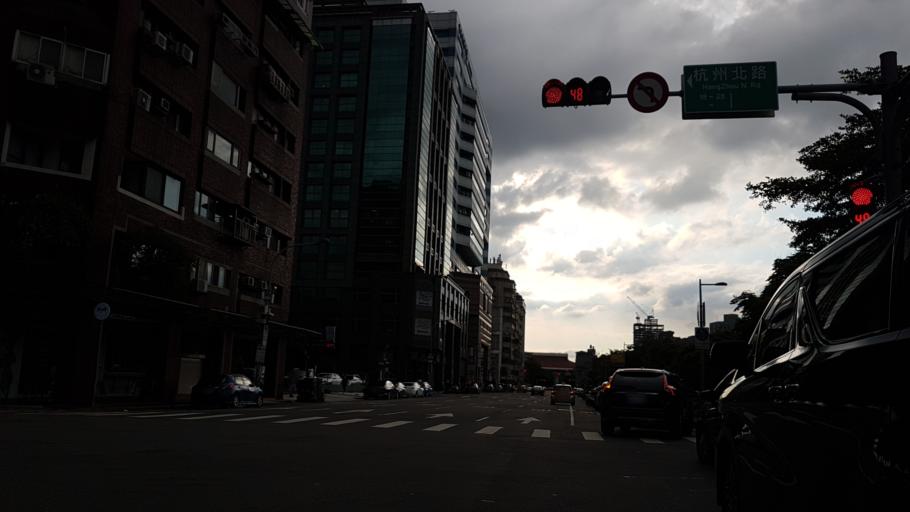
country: TW
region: Taipei
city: Taipei
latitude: 25.0455
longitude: 121.5274
